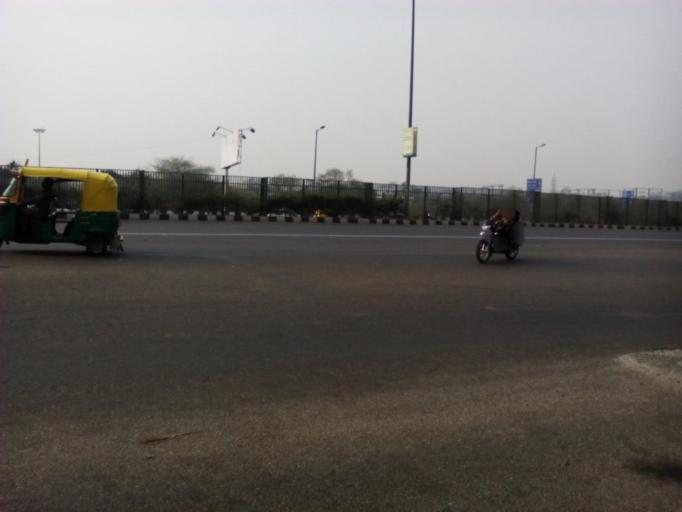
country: IN
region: Uttar Pradesh
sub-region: Gautam Buddha Nagar
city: Noida
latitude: 28.6492
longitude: 77.3190
